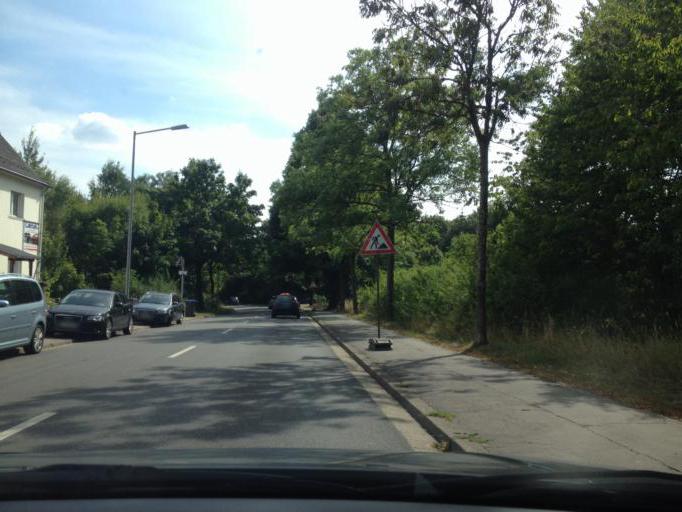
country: DE
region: Saarland
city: Neunkirchen
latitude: 49.3318
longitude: 7.1865
